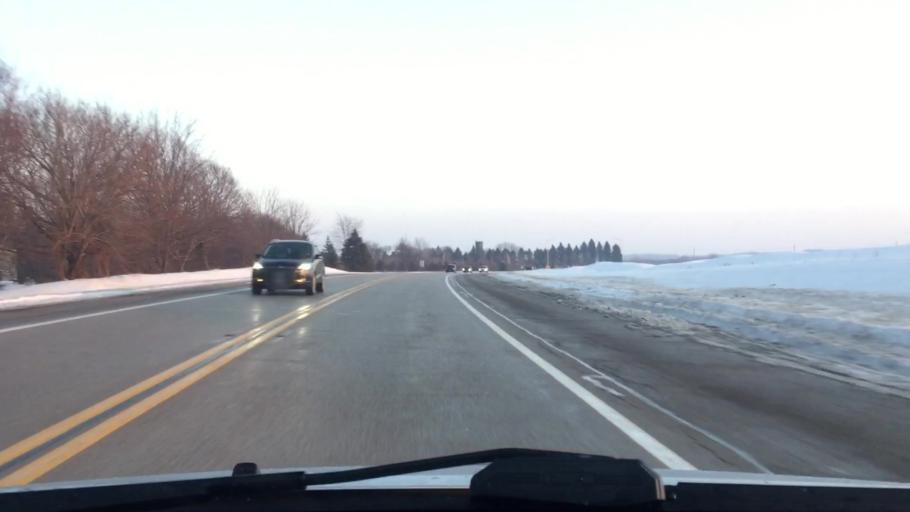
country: US
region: Illinois
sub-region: Kane County
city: Wasco
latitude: 41.9447
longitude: -88.4004
